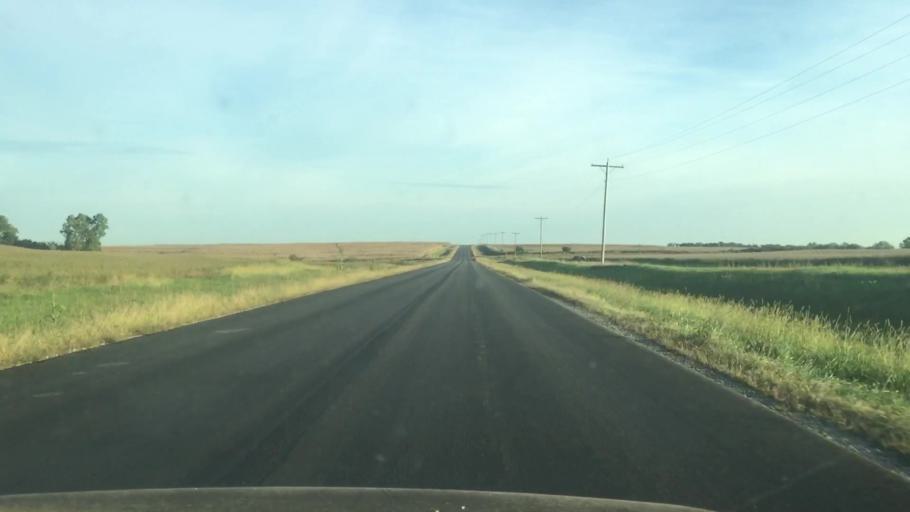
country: US
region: Kansas
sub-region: Marshall County
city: Marysville
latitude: 39.9115
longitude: -96.6008
